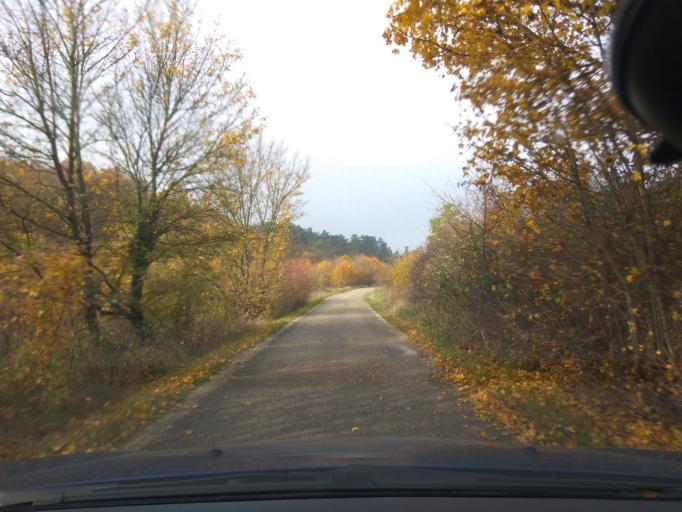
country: SK
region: Trnavsky
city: Vrbove
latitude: 48.6812
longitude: 17.7058
